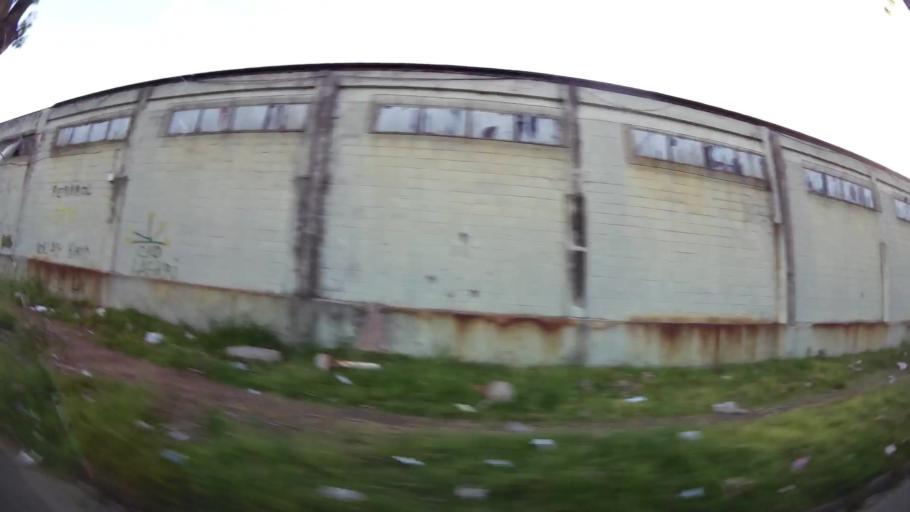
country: UY
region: Montevideo
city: Montevideo
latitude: -34.8452
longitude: -56.1611
